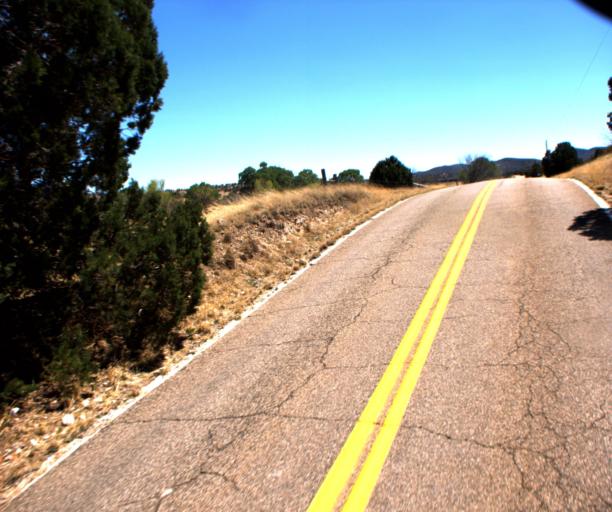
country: US
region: Arizona
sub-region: Cochise County
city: Huachuca City
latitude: 31.5536
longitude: -110.5289
